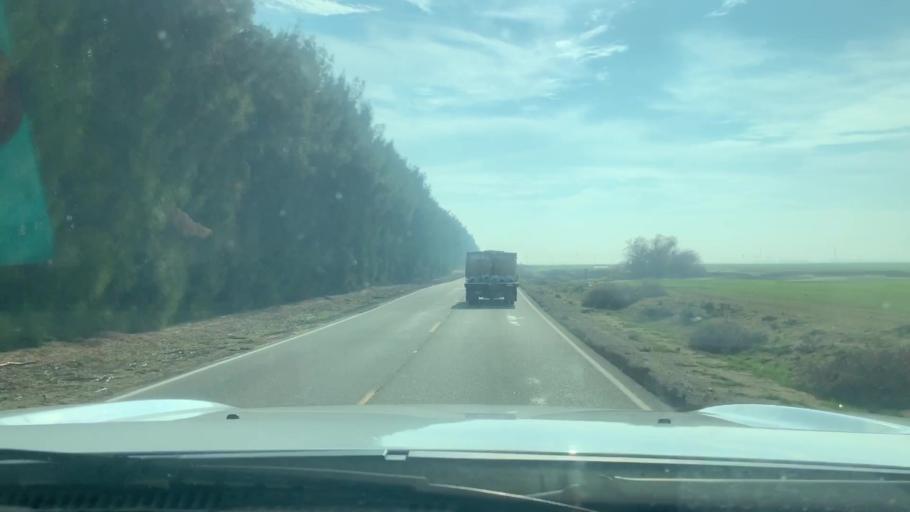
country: US
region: California
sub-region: Kern County
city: Lost Hills
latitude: 35.5077
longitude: -119.7459
